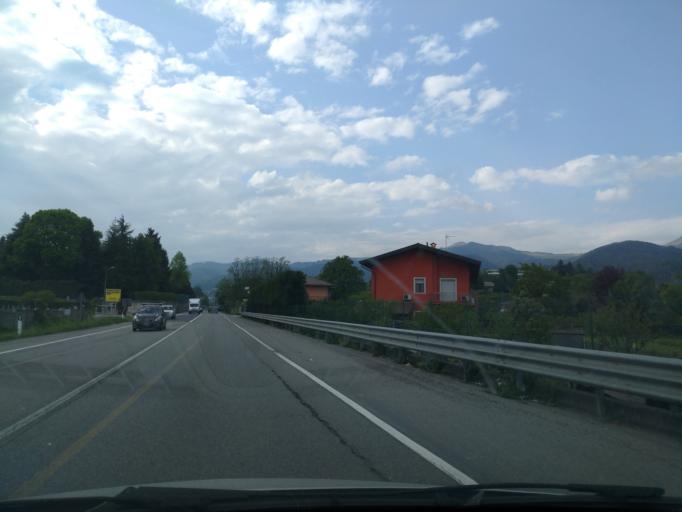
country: IT
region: Lombardy
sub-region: Provincia di Como
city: Albese Con Cassano
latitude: 45.7853
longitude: 9.1625
